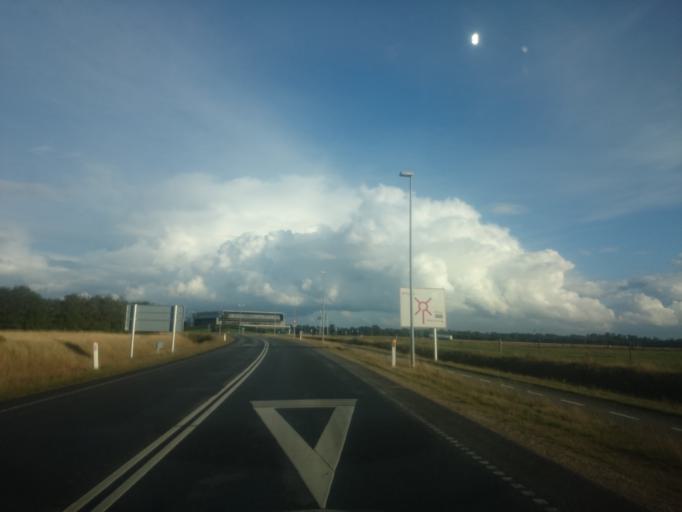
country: DK
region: South Denmark
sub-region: Billund Kommune
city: Billund
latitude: 55.7378
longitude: 9.0922
